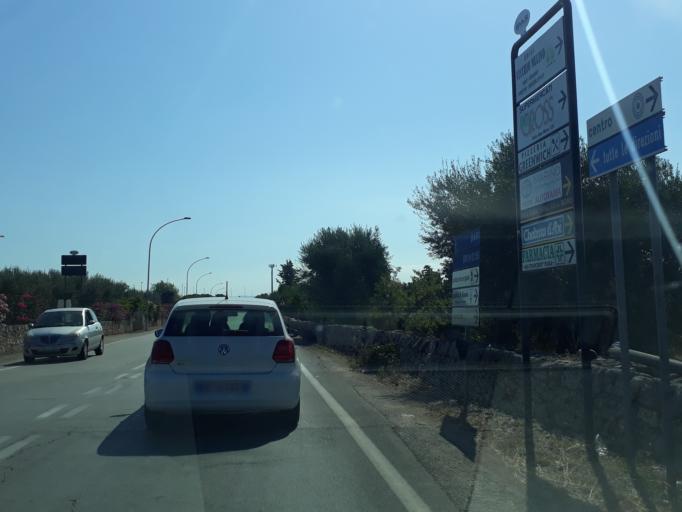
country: IT
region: Apulia
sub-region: Provincia di Bari
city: Monopoli
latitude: 40.9275
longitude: 17.3135
